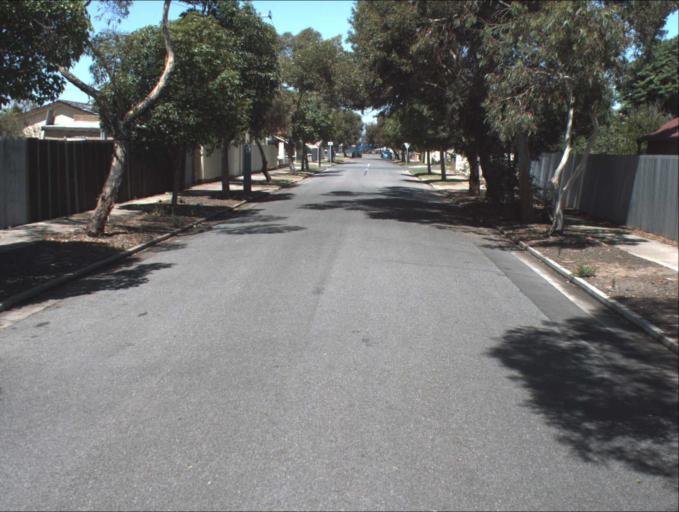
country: AU
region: South Australia
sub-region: Port Adelaide Enfield
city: Alberton
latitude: -34.8497
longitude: 138.5310
